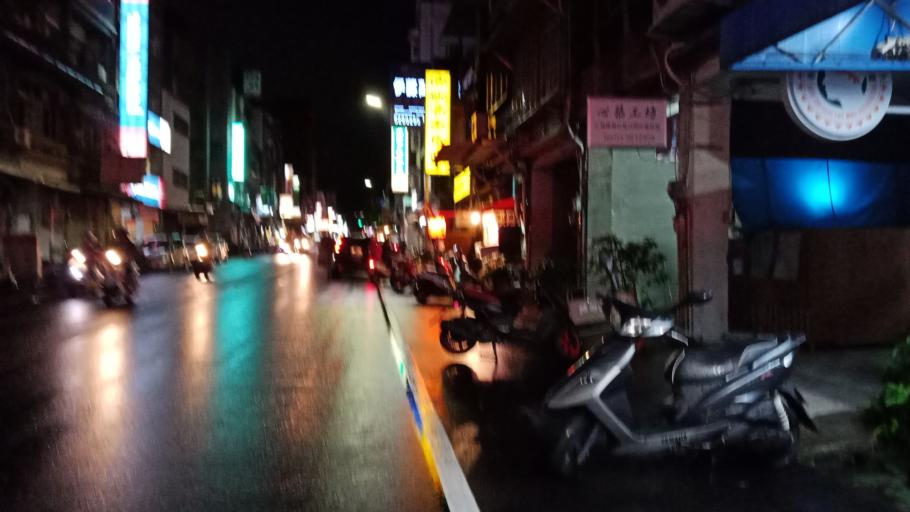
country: TW
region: Taiwan
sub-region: Hsinchu
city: Hsinchu
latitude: 24.7978
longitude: 120.9740
